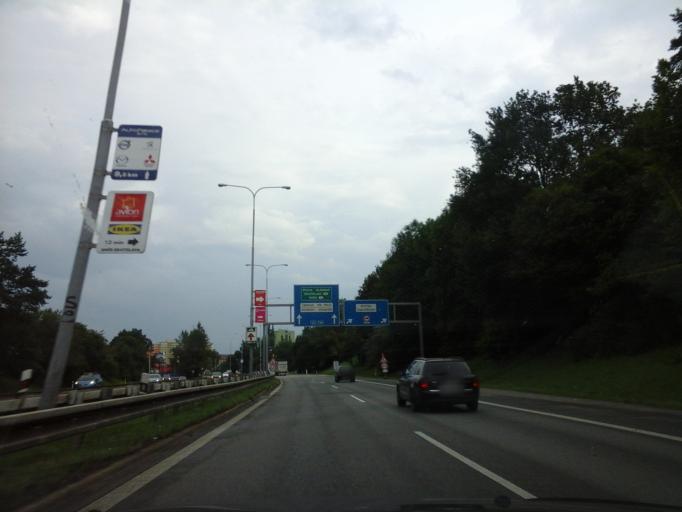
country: CZ
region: South Moravian
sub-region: Mesto Brno
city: Mokra Hora
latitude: 49.2397
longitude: 16.5891
